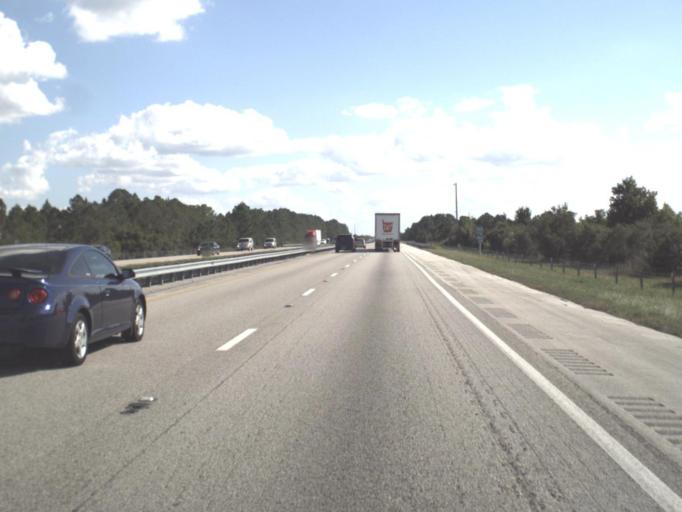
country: US
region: Florida
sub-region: Brevard County
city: June Park
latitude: 27.9072
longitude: -81.0487
